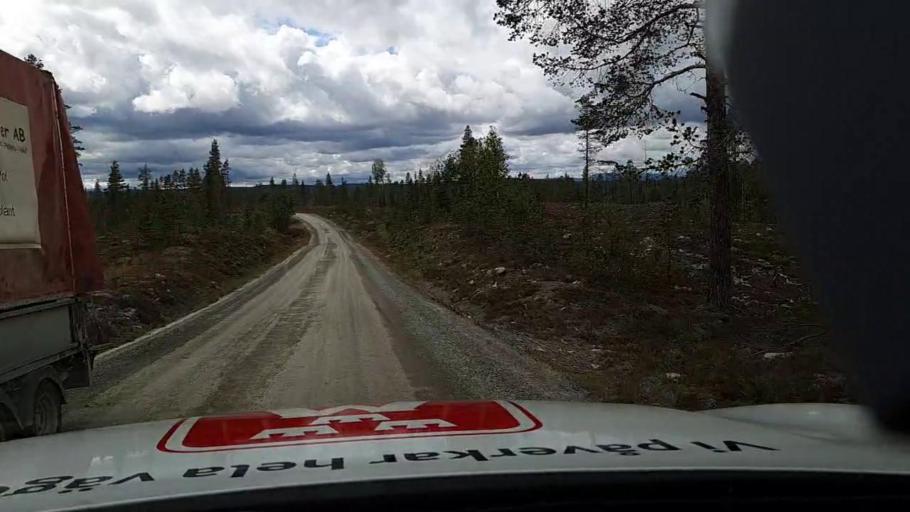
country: SE
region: Jaemtland
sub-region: Are Kommun
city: Jarpen
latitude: 62.8090
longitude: 13.8069
